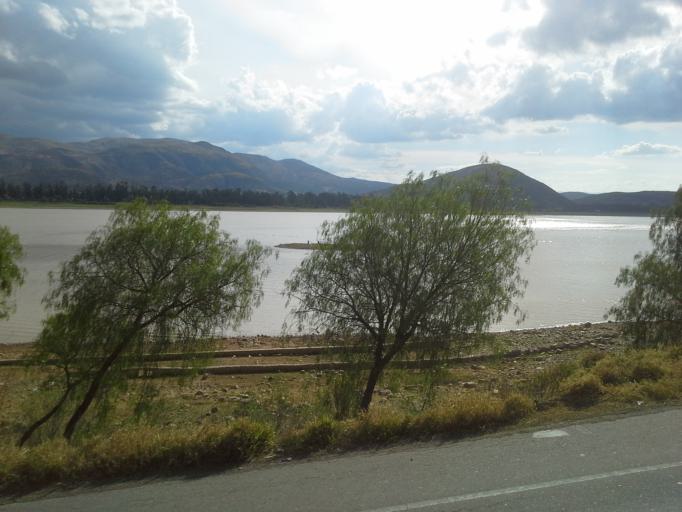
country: BO
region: Cochabamba
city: Tarata
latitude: -17.5336
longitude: -66.0830
